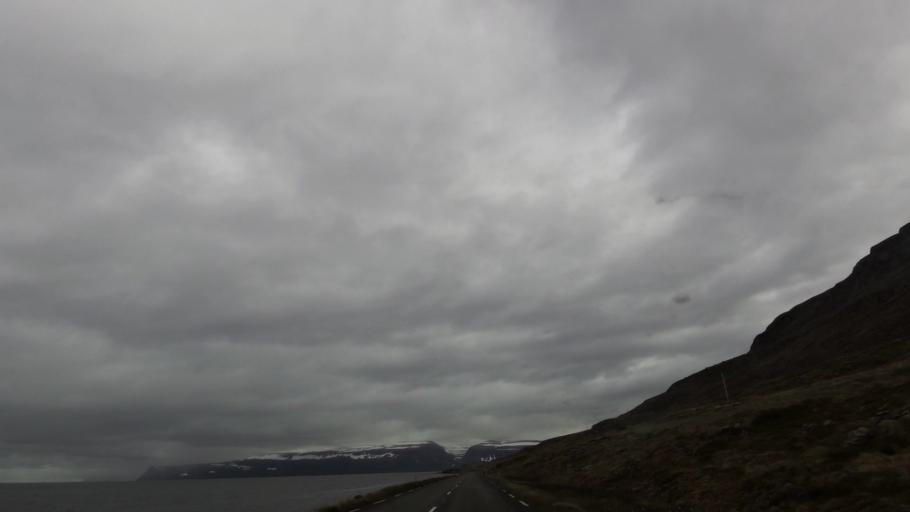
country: IS
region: Westfjords
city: Isafjoerdur
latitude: 66.0341
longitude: -22.7740
